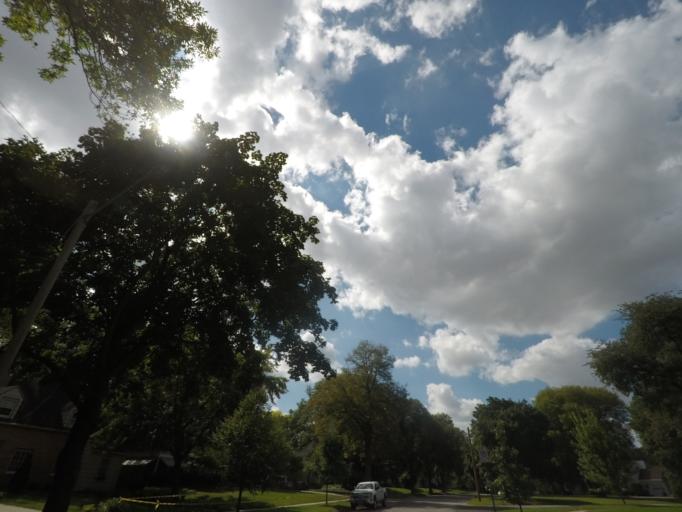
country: US
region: Iowa
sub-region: Story County
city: Ames
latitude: 42.0161
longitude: -93.6402
